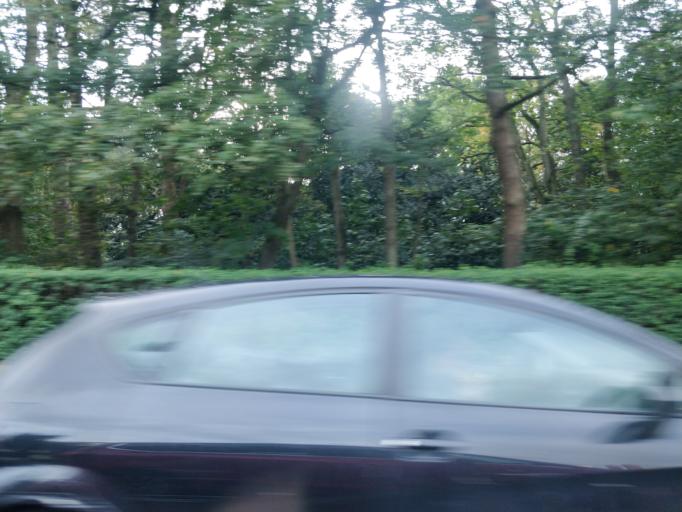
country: GB
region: England
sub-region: Sefton
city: Southport
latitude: 53.6576
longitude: -2.9844
